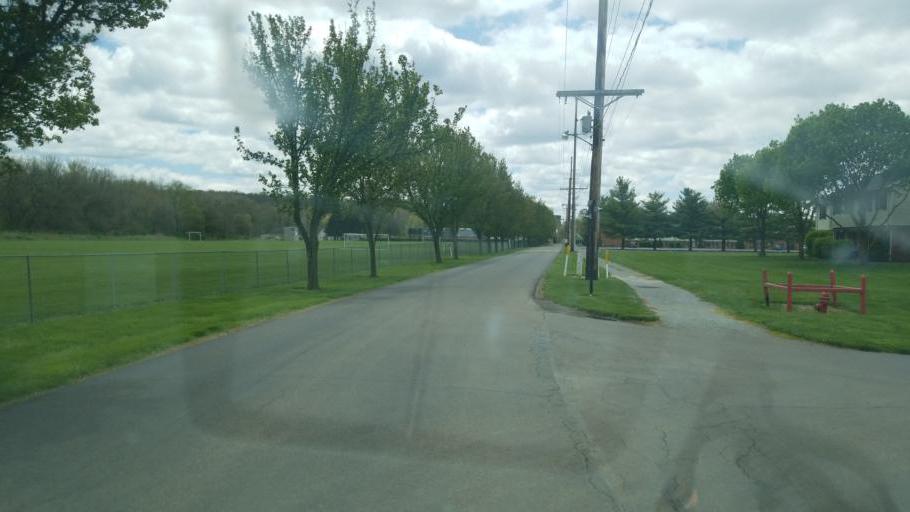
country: US
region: Ohio
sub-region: Knox County
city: Mount Vernon
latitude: 40.3777
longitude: -82.4684
